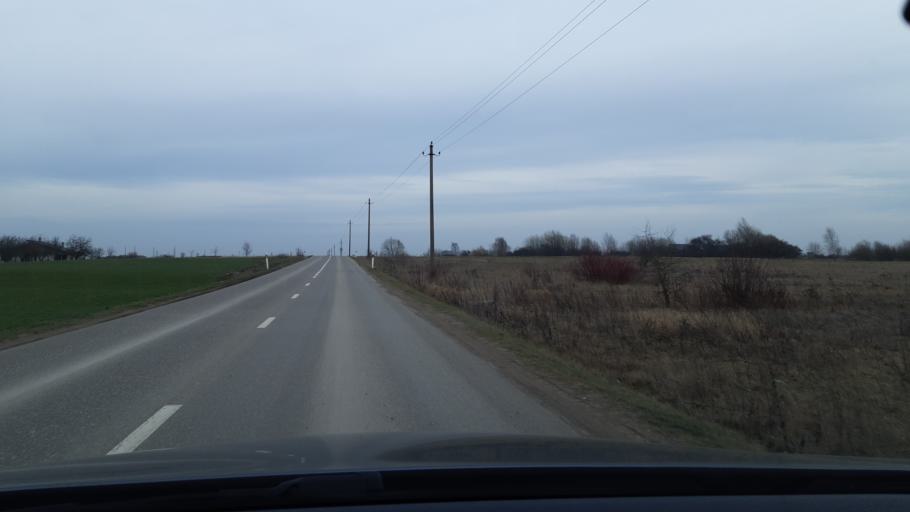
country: LT
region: Kauno apskritis
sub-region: Kaunas
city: Sargenai
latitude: 54.9484
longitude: 23.8339
